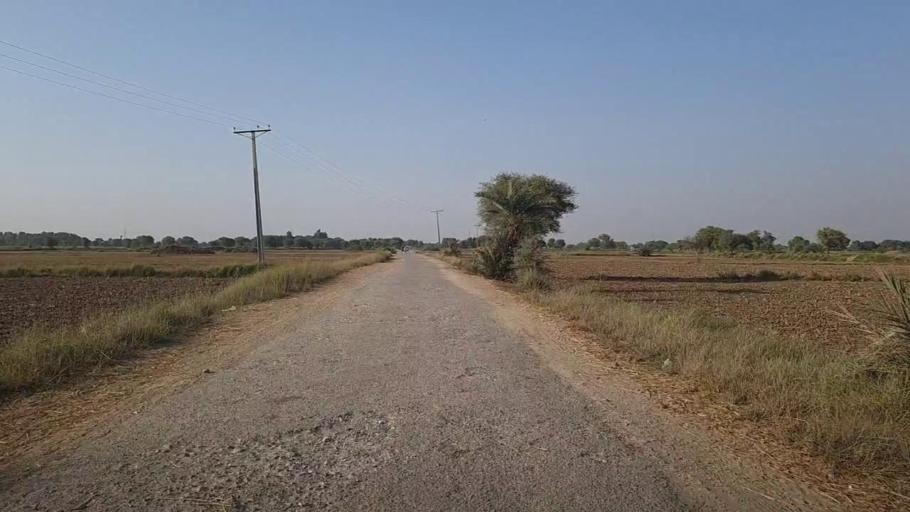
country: PK
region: Sindh
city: Kashmor
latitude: 28.4179
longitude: 69.4098
